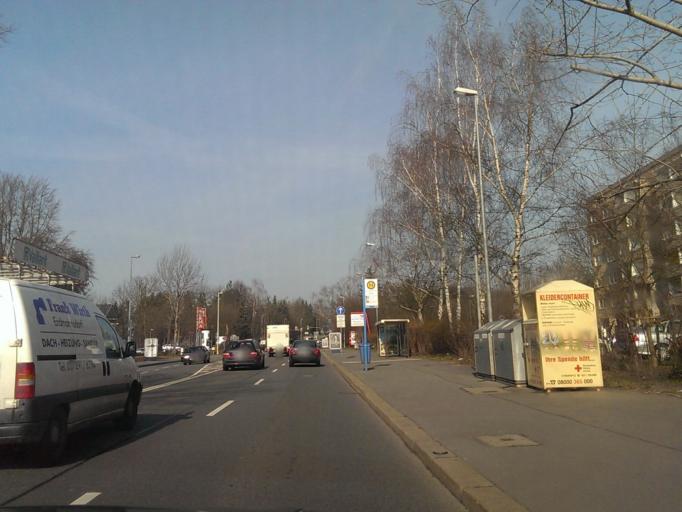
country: DE
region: Saxony
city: Wittgensdorf
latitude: 50.8528
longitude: 12.8851
